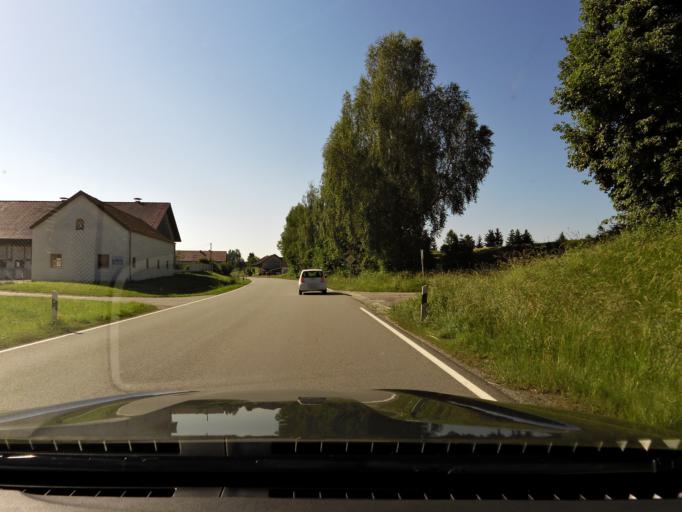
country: DE
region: Bavaria
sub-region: Upper Bavaria
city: Egglkofen
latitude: 48.3857
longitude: 12.4609
